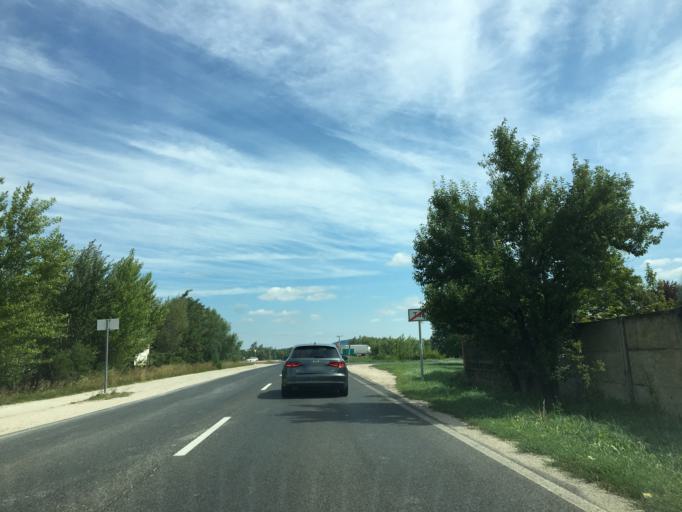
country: HU
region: Komarom-Esztergom
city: Tat
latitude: 47.7436
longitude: 18.6625
